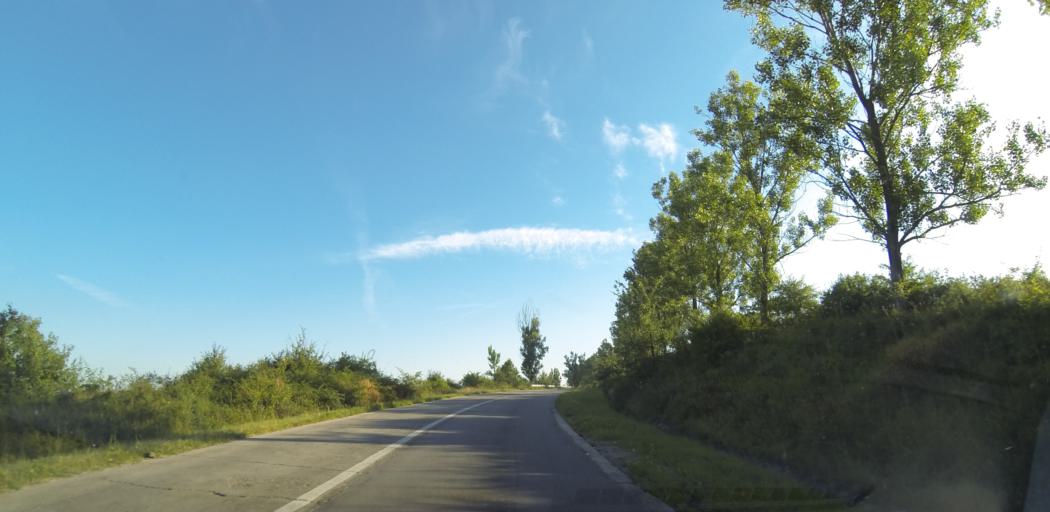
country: RO
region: Dolj
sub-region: Comuna Bulzesti
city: Bulzesti
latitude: 44.5318
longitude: 23.9022
